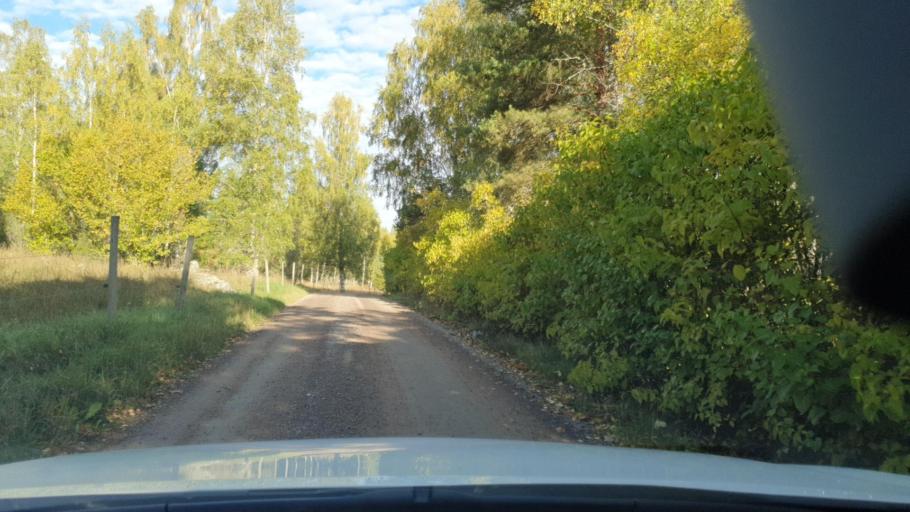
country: SE
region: Kalmar
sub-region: Hultsfreds Kommun
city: Malilla
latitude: 57.3178
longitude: 15.8114
